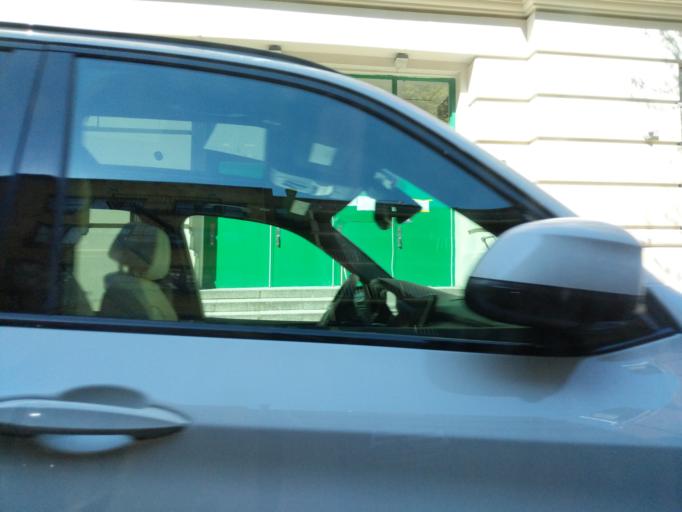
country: US
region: New York
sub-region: New York County
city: Manhattan
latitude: 40.7777
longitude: -73.9473
